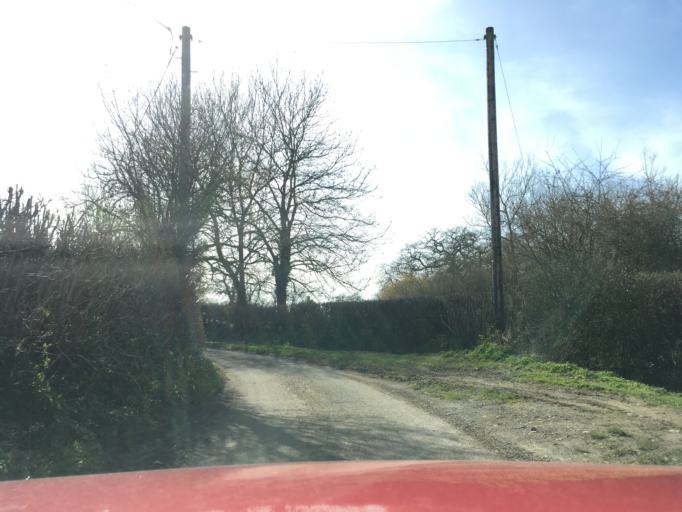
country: GB
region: England
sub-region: Wiltshire
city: Chippenham
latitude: 51.4987
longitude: -2.1495
